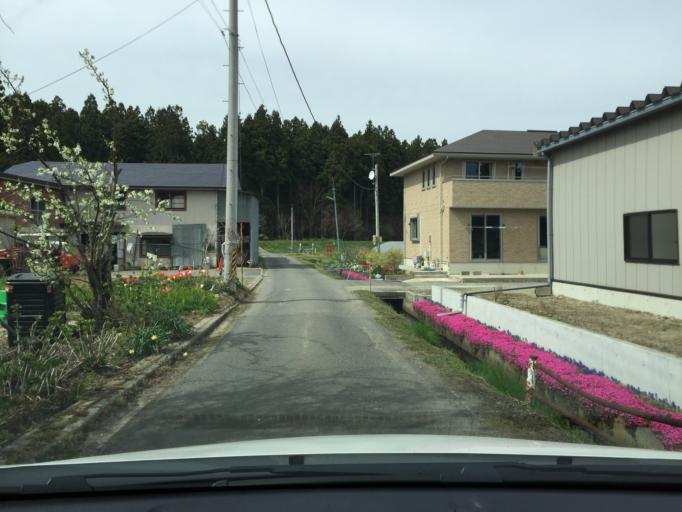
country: JP
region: Fukushima
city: Inawashiro
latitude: 37.5191
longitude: 140.1323
